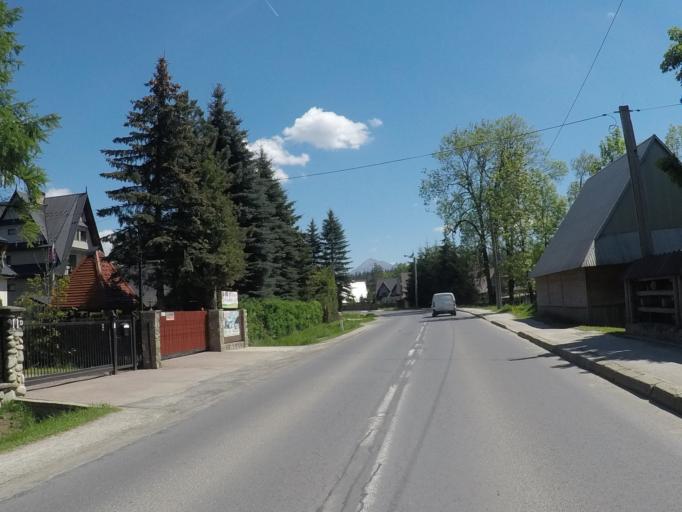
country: PL
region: Lesser Poland Voivodeship
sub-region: Powiat tatrzanski
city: Poronin
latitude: 49.3325
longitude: 20.0122
